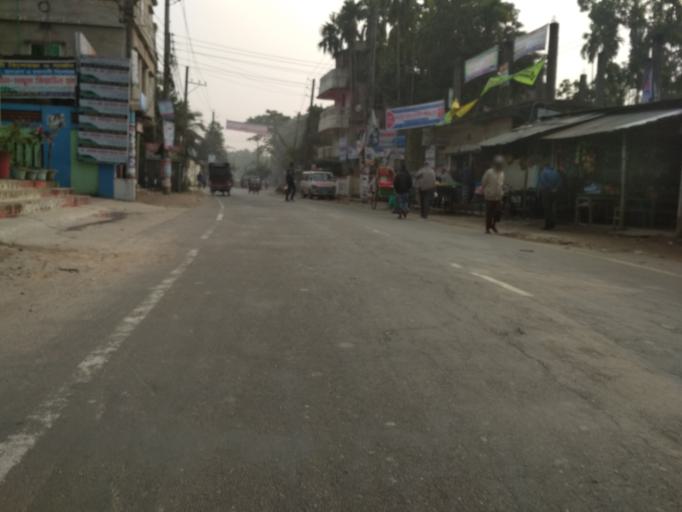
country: BD
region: Chittagong
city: Lakshmipur
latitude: 22.9394
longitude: 90.8415
